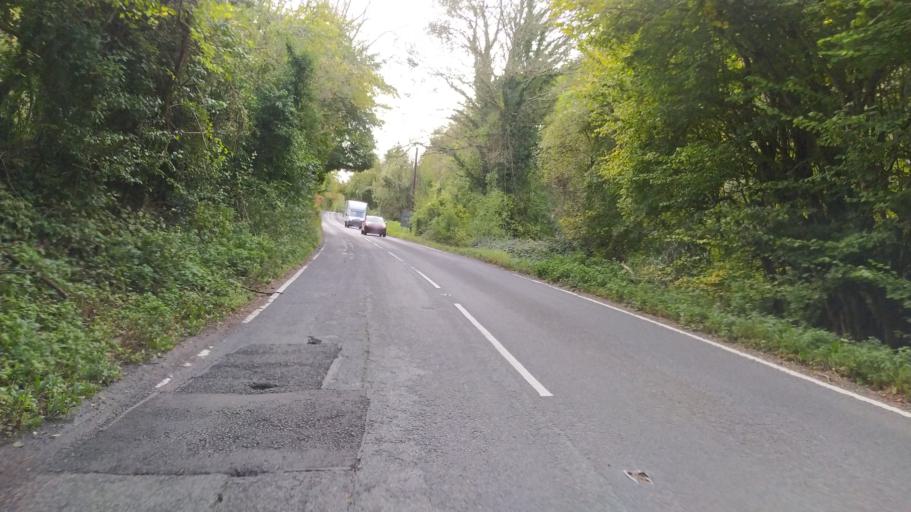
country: GB
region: England
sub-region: Hampshire
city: Romsey
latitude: 51.0480
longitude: -1.5180
